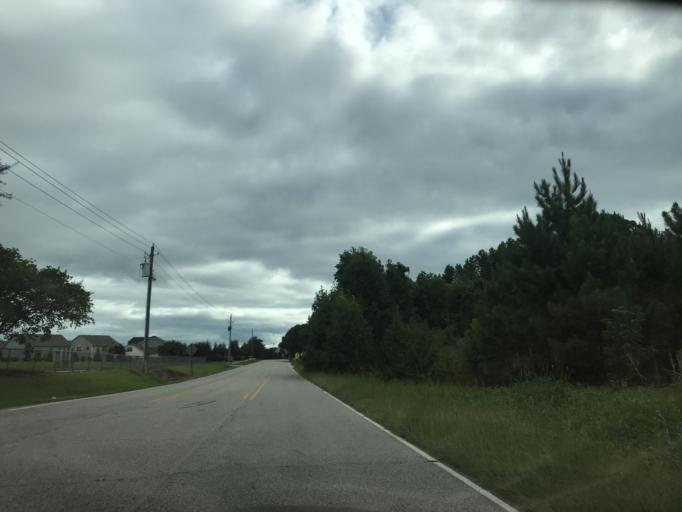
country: US
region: North Carolina
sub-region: Johnston County
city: Clayton
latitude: 35.5792
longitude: -78.5442
